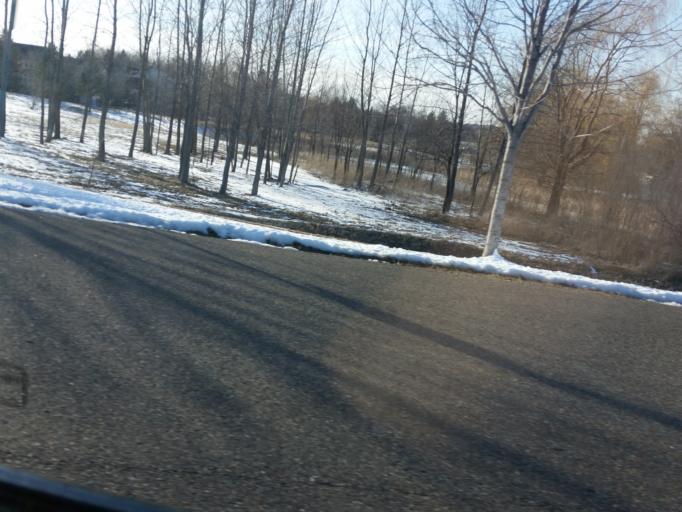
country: US
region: Minnesota
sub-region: Scott County
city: Elko New Market
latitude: 44.6329
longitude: -93.3669
